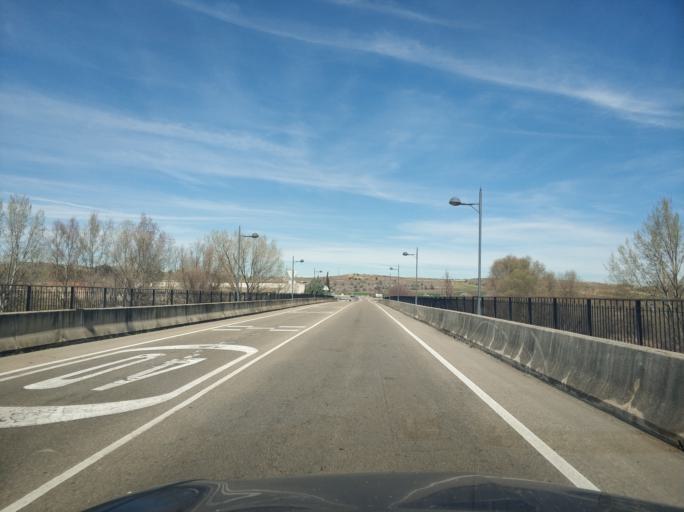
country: ES
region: Castille and Leon
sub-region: Provincia de Valladolid
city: Simancas
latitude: 41.5890
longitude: -4.8181
